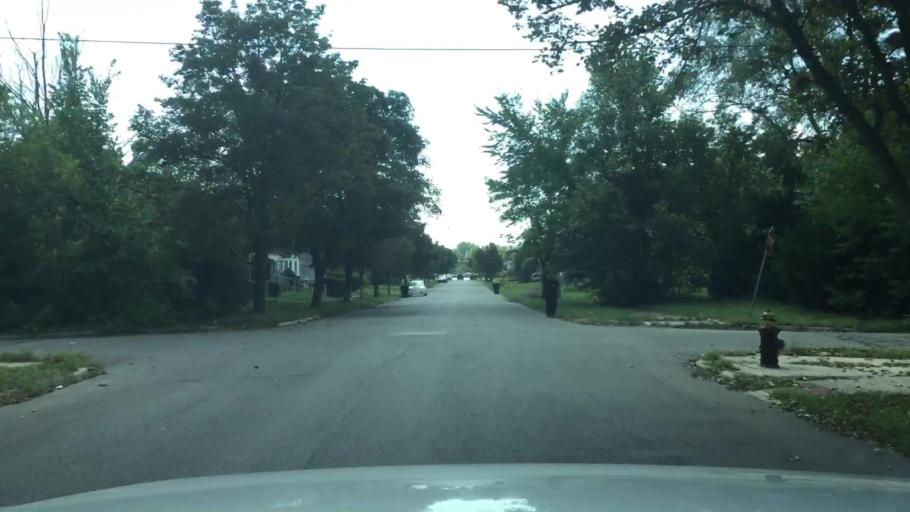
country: US
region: Michigan
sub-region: Wayne County
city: Dearborn
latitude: 42.3556
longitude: -83.1463
